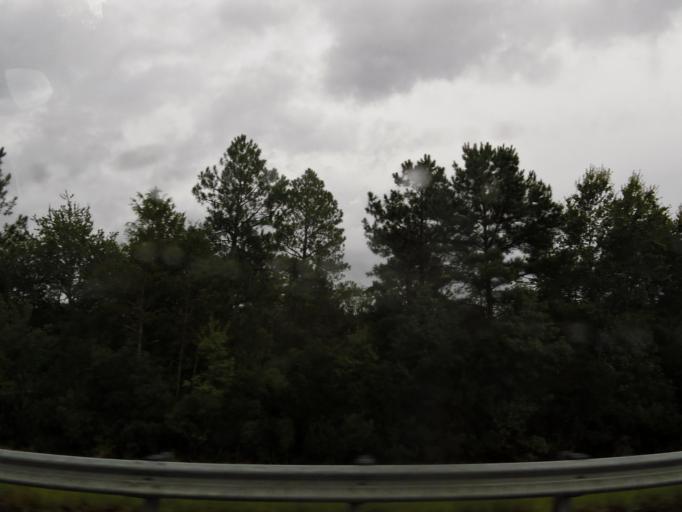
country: US
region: Georgia
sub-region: Wayne County
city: Jesup
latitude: 31.5712
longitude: -81.8428
